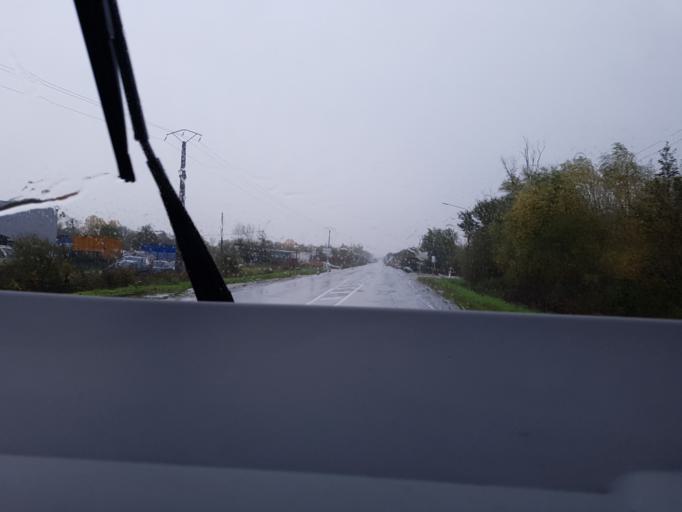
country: FR
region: Aquitaine
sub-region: Departement de la Gironde
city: Saint-Louis-de-Montferrand
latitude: 44.9392
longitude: -0.5238
